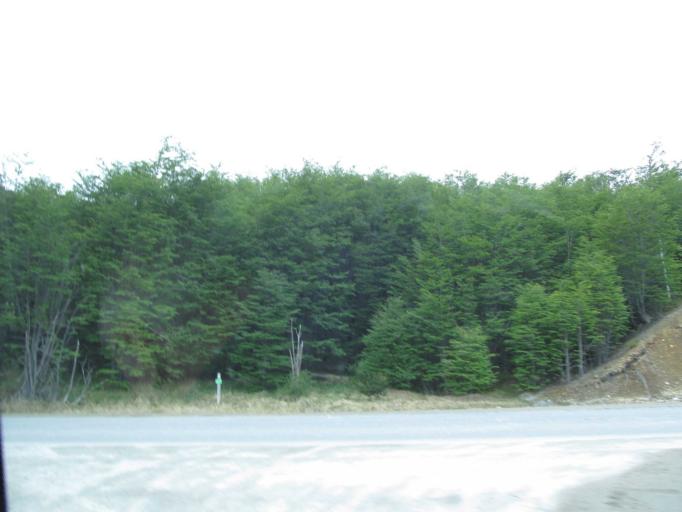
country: AR
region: Tierra del Fuego
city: Ushuaia
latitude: -54.7409
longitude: -67.8310
